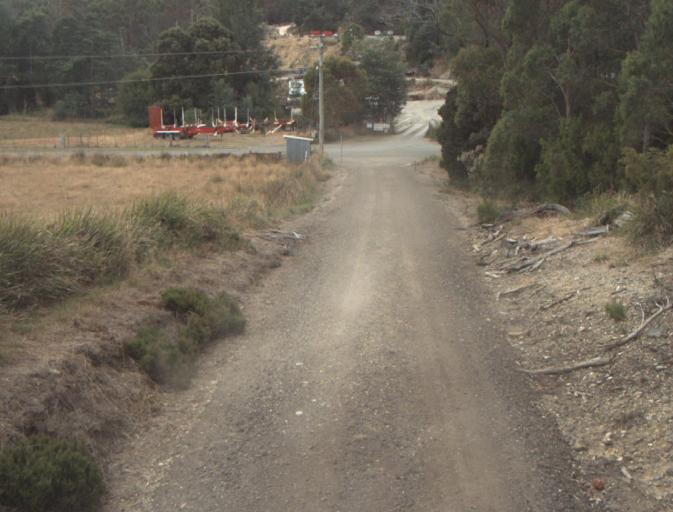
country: AU
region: Tasmania
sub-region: Launceston
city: Mayfield
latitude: -41.2383
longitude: 147.1864
